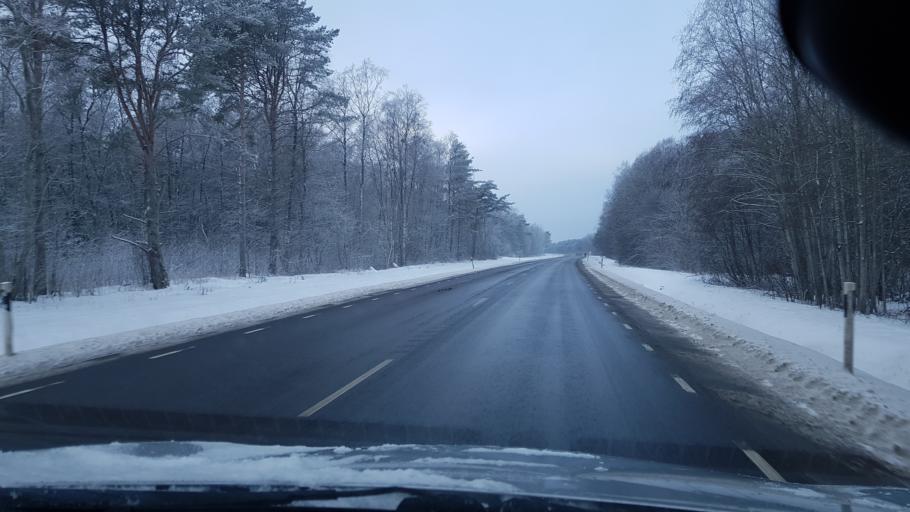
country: EE
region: Harju
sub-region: Paldiski linn
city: Paldiski
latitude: 59.3380
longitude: 24.2238
